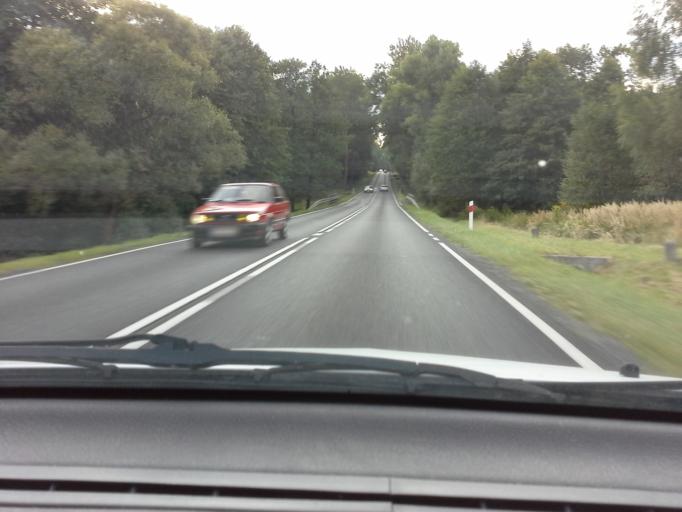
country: PL
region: Lesser Poland Voivodeship
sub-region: Powiat krakowski
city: Filipowice
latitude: 50.1395
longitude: 19.5561
